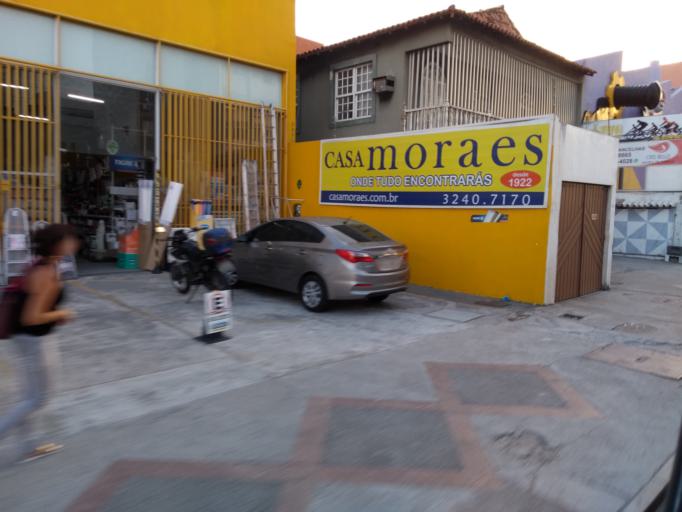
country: BR
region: Bahia
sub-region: Salvador
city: Salvador
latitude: -13.0118
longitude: -38.4693
